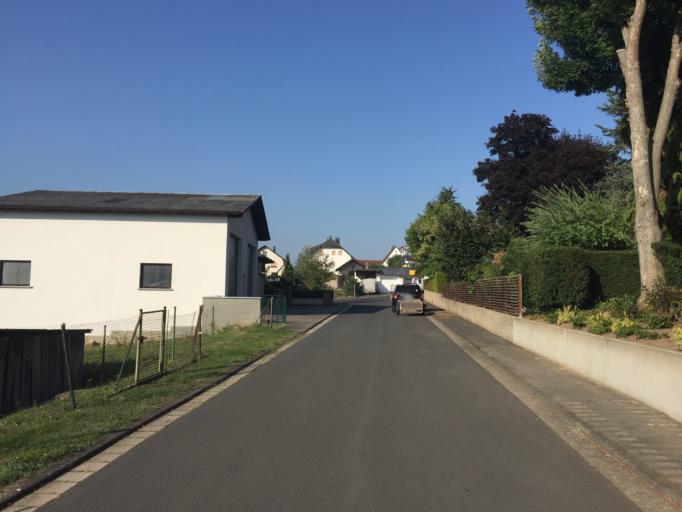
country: DE
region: Hesse
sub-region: Regierungsbezirk Giessen
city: Hoernsheim
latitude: 50.4631
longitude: 8.5874
